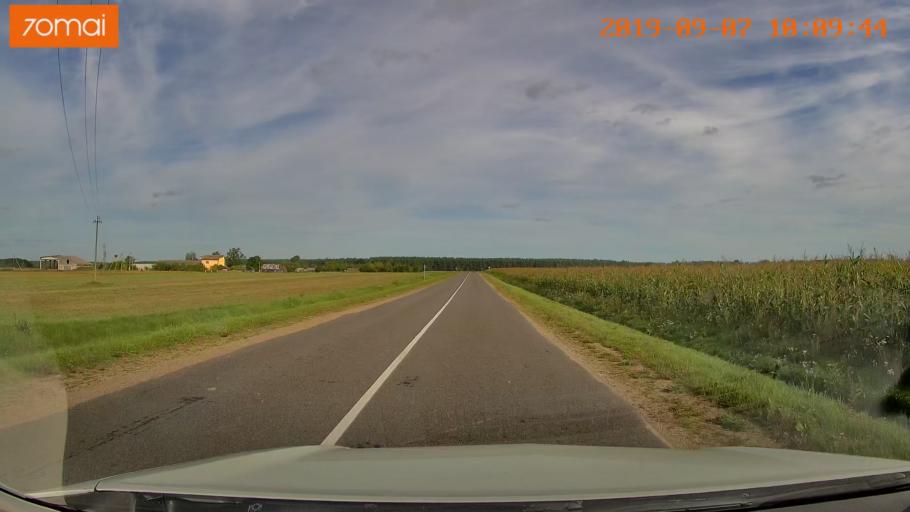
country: BY
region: Grodnenskaya
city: Voranava
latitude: 54.0991
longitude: 25.3725
